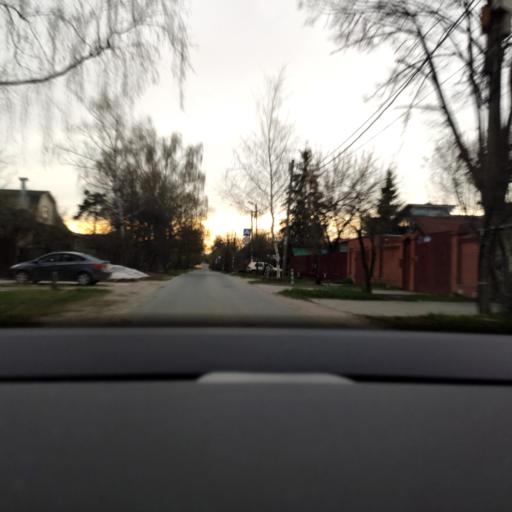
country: RU
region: Moskovskaya
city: Reutov
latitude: 55.7717
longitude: 37.8920
